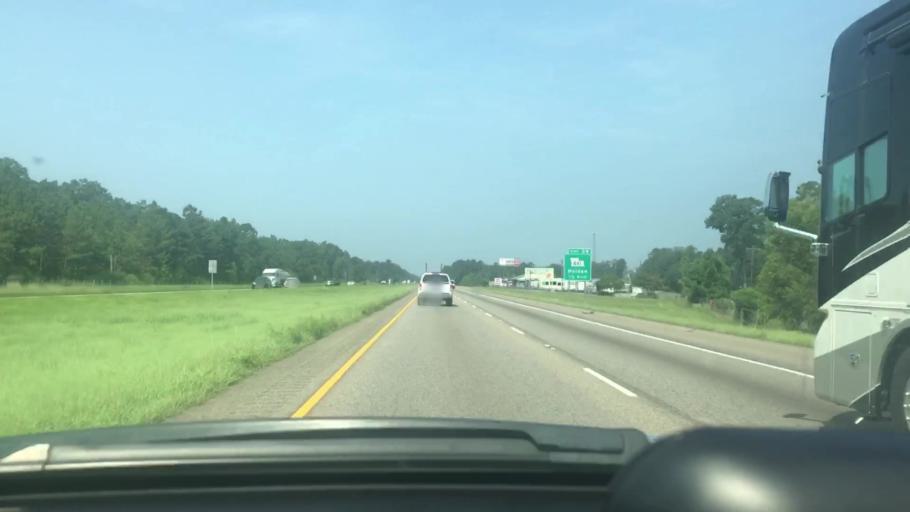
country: US
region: Louisiana
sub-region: Livingston Parish
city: Albany
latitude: 30.4748
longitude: -90.6299
